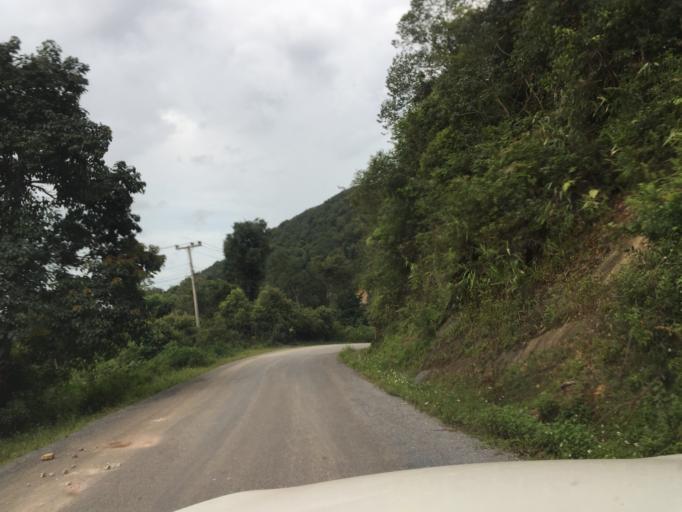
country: LA
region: Phongsali
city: Phongsali
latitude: 21.3146
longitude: 102.0477
